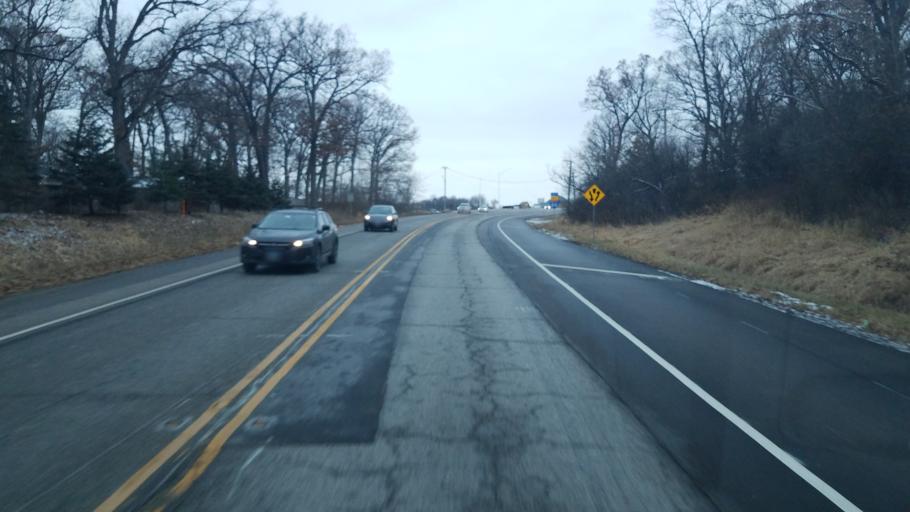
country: US
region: Illinois
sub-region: Kane County
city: Sugar Grove
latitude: 41.8148
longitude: -88.4647
